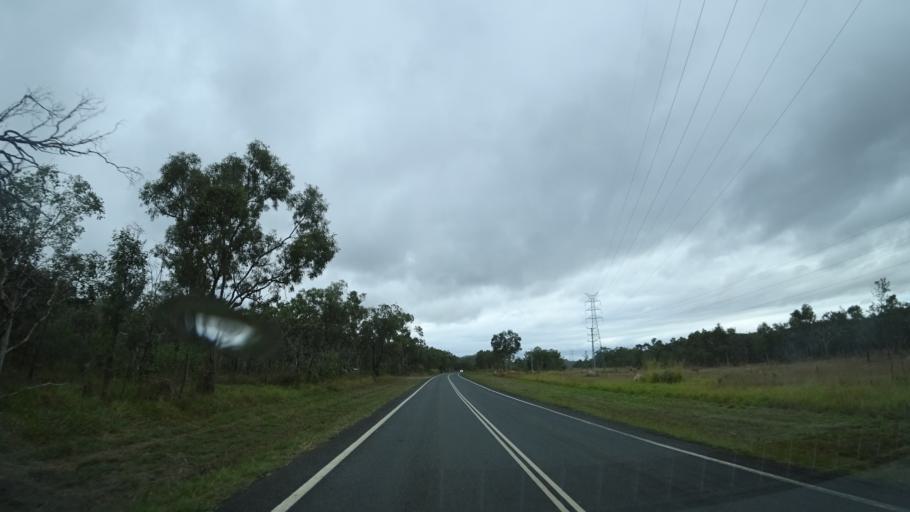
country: AU
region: Queensland
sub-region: Cairns
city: Port Douglas
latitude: -16.7177
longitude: 145.3528
